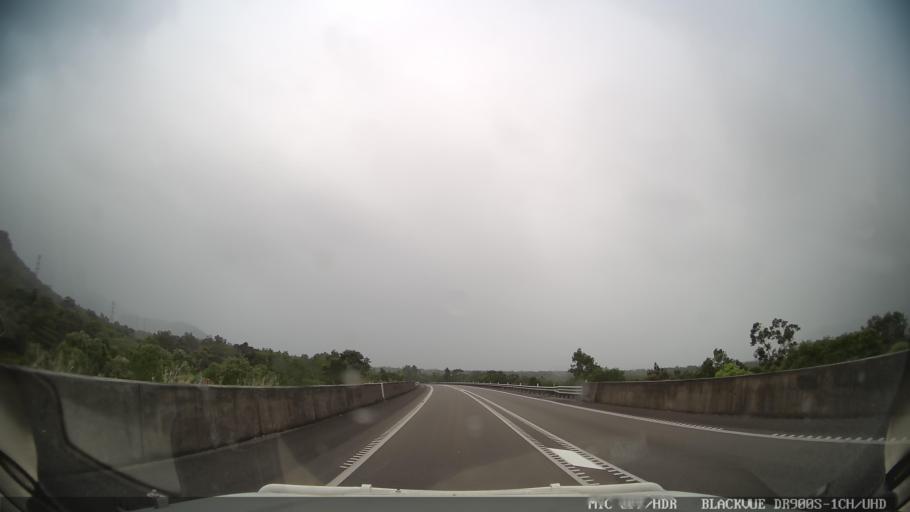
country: AU
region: Queensland
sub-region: Hinchinbrook
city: Ingham
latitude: -18.5100
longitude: 146.1878
